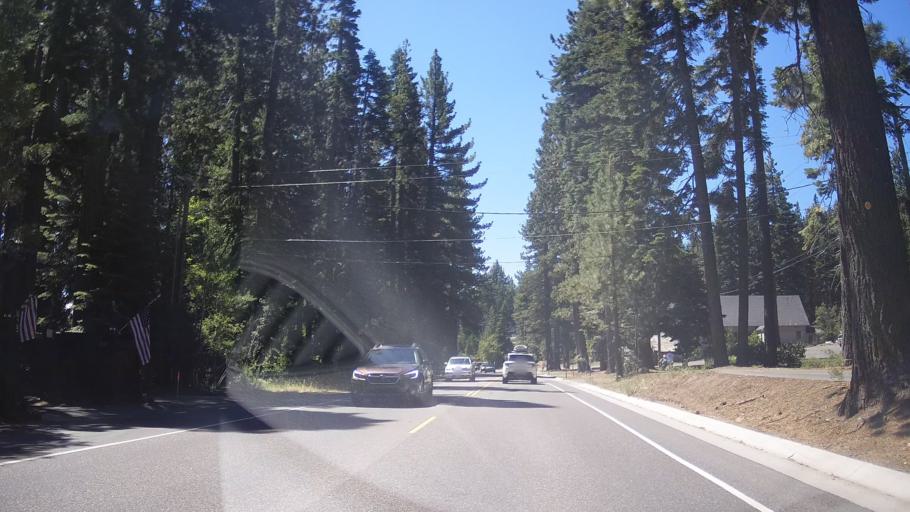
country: US
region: California
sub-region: Placer County
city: Sunnyside-Tahoe City
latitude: 39.1538
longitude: -120.1460
